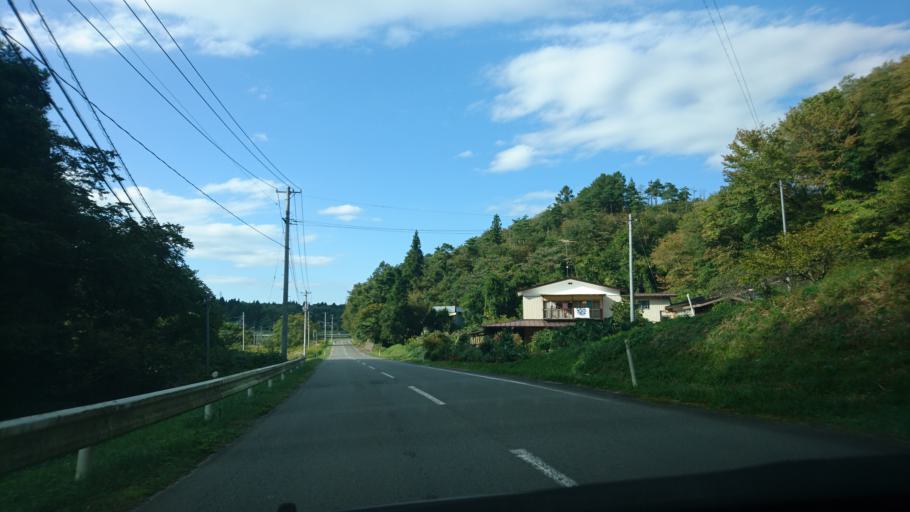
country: JP
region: Iwate
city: Ichinoseki
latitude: 38.8735
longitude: 141.3442
